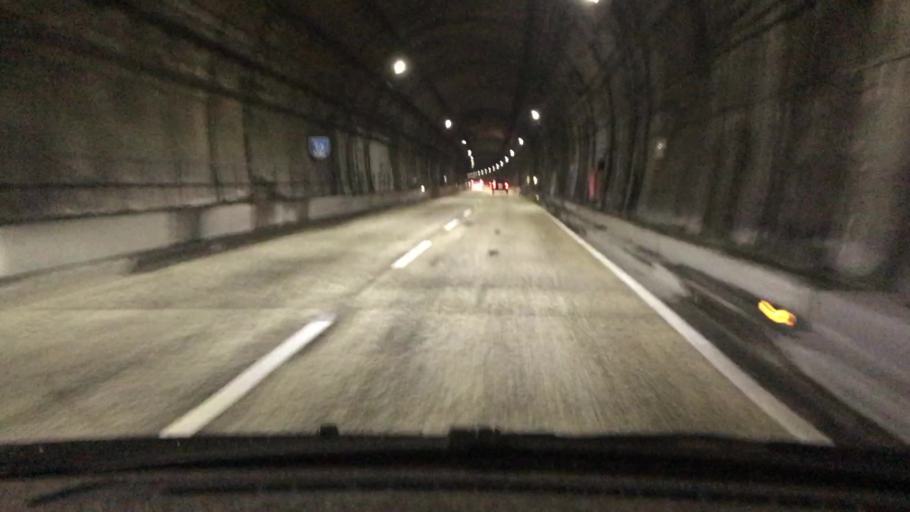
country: JP
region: Hyogo
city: Kobe
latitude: 34.7238
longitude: 135.1840
